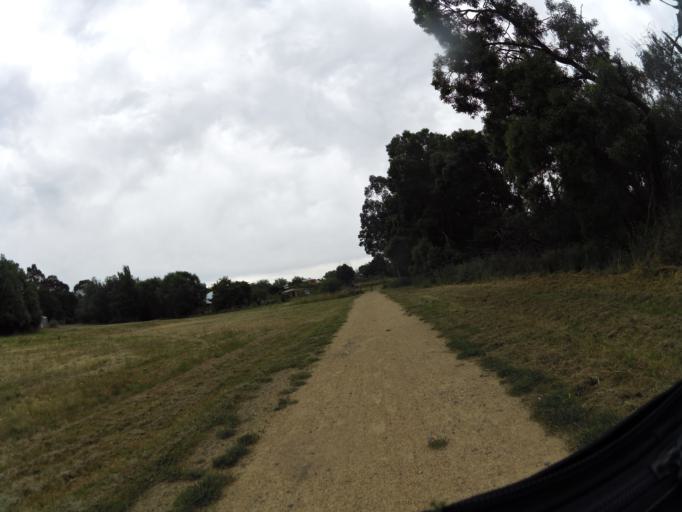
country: AU
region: Victoria
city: Brown Hill
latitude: -37.4271
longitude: 143.8978
